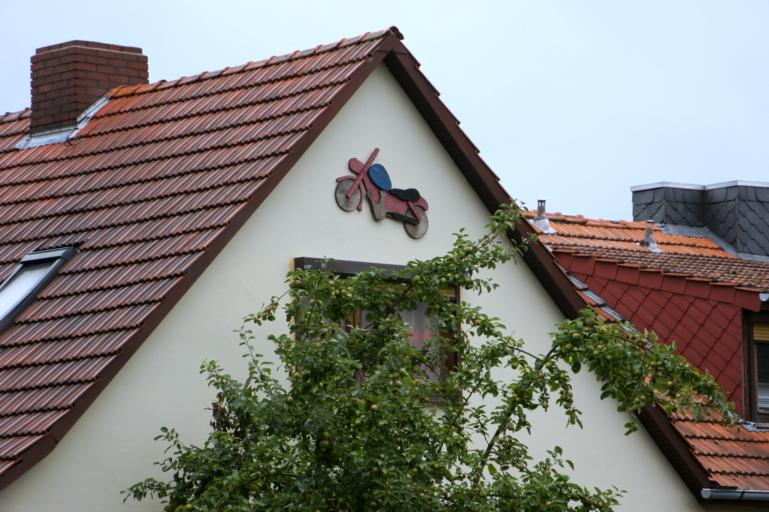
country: DE
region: Lower Saxony
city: Stuhr
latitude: 53.0912
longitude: 8.7488
